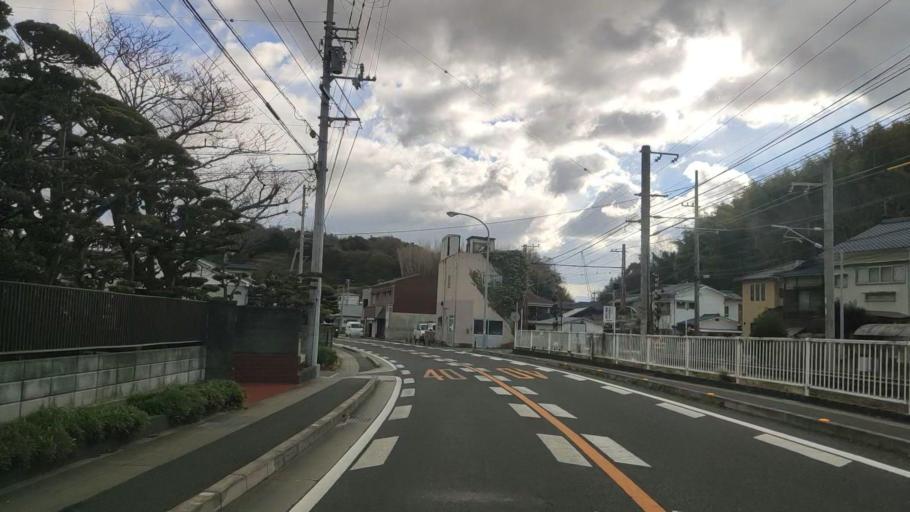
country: JP
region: Ehime
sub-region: Shikoku-chuo Shi
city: Matsuyama
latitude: 33.8700
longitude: 132.7112
